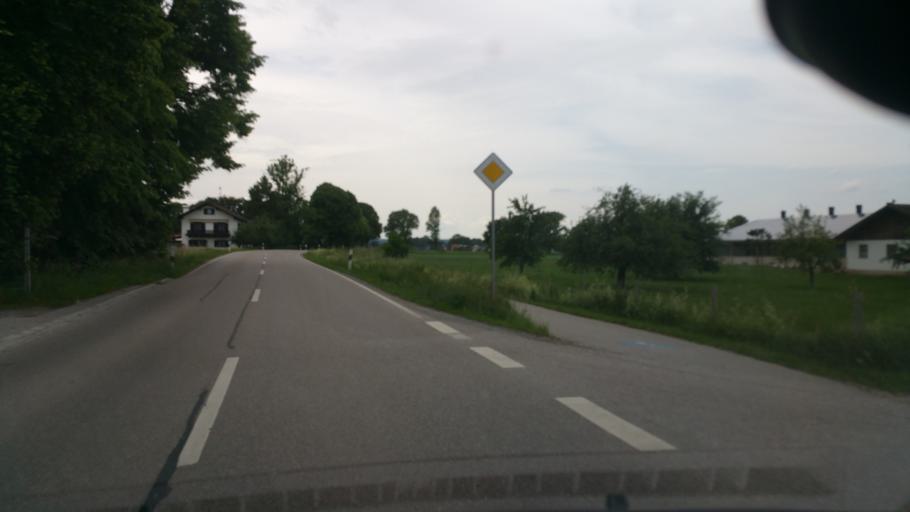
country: DE
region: Bavaria
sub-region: Upper Bavaria
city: Bruckmuhl
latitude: 47.8650
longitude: 11.9346
